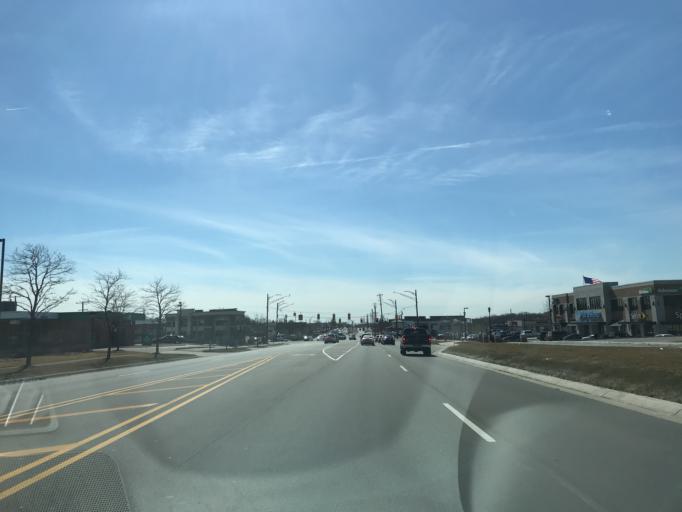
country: US
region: Michigan
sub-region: Oakland County
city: West Bloomfield Township
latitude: 42.5448
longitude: -83.3608
